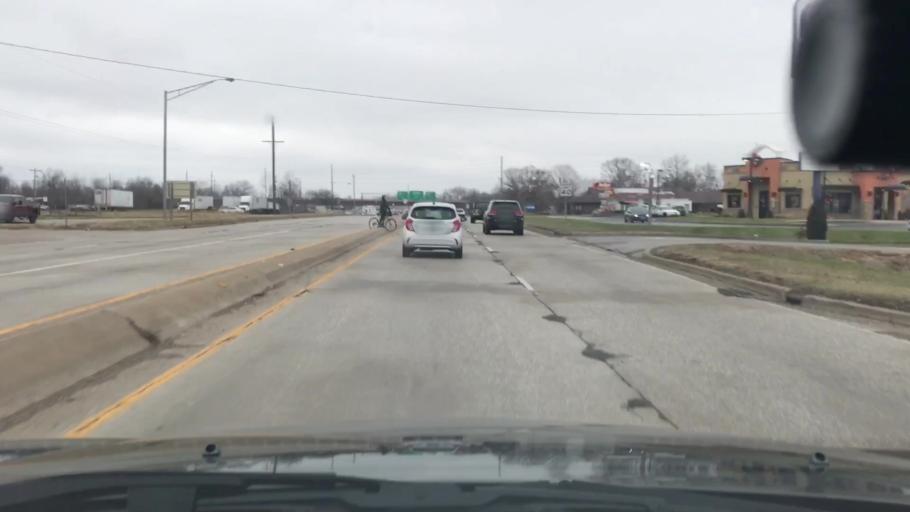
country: US
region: Illinois
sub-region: Madison County
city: Bethalto
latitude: 38.9013
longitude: -90.0599
